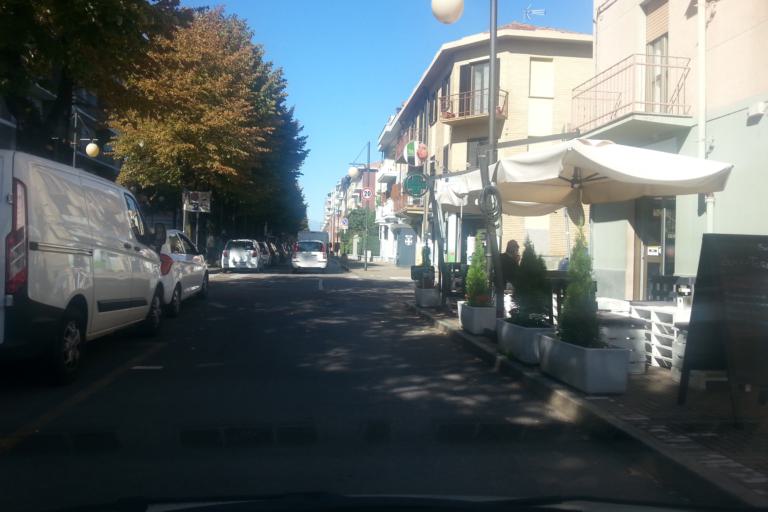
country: IT
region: Piedmont
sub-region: Provincia di Torino
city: Collegno
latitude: 45.0747
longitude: 7.5741
